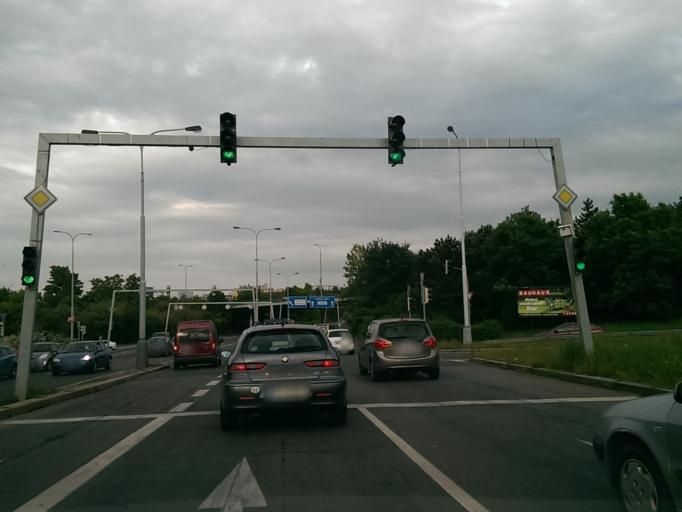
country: CZ
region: Central Bohemia
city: Vestec
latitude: 50.0411
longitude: 14.4863
